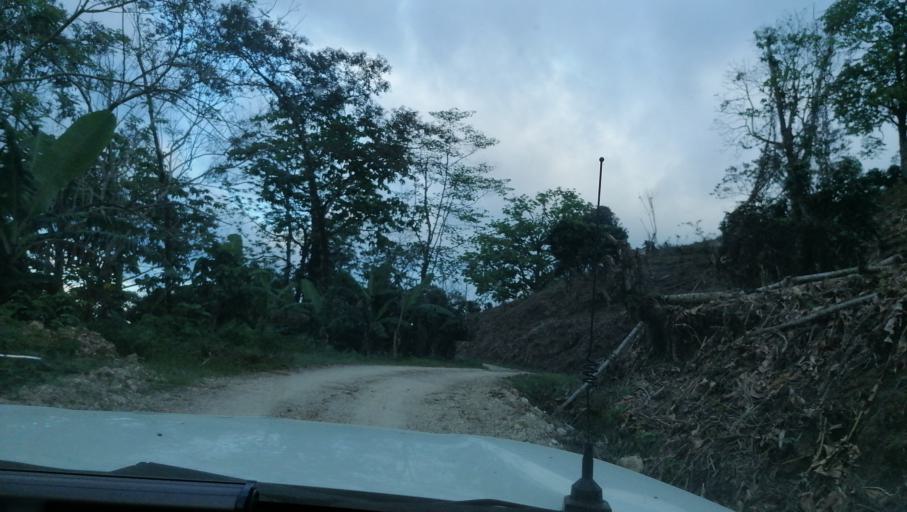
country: MX
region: Chiapas
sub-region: Francisco Leon
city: San Miguel la Sardina
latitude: 17.3075
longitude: -93.2674
